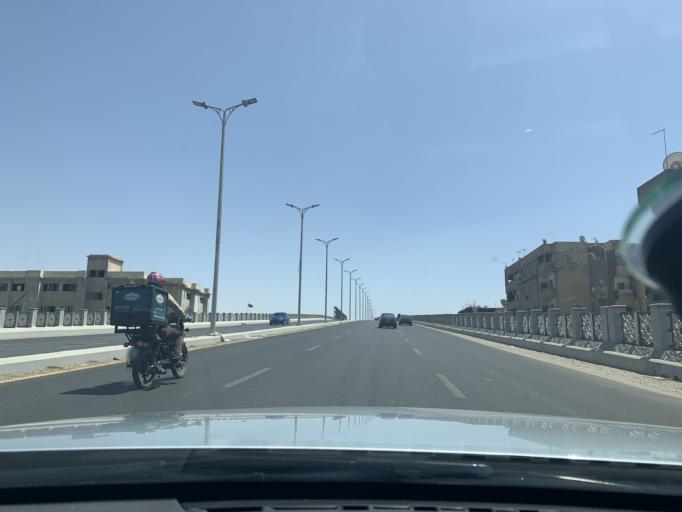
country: EG
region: Muhafazat al Qahirah
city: Cairo
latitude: 30.0977
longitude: 31.3426
